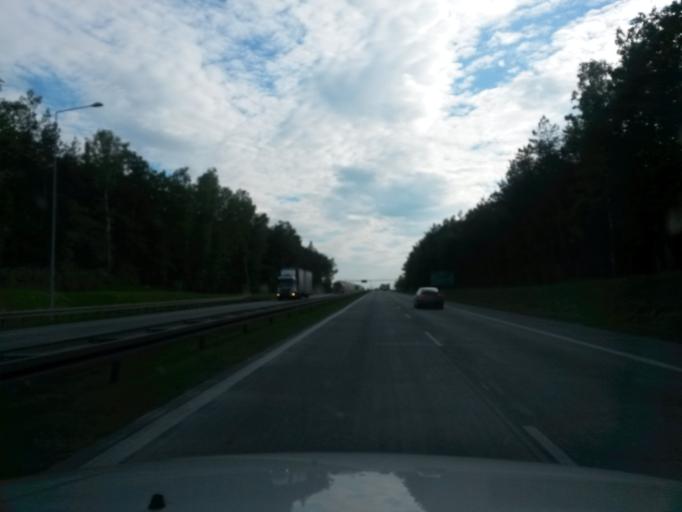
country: PL
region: Lodz Voivodeship
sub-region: Powiat tomaszowski
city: Tomaszow Mazowiecki
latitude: 51.5628
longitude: 20.0168
